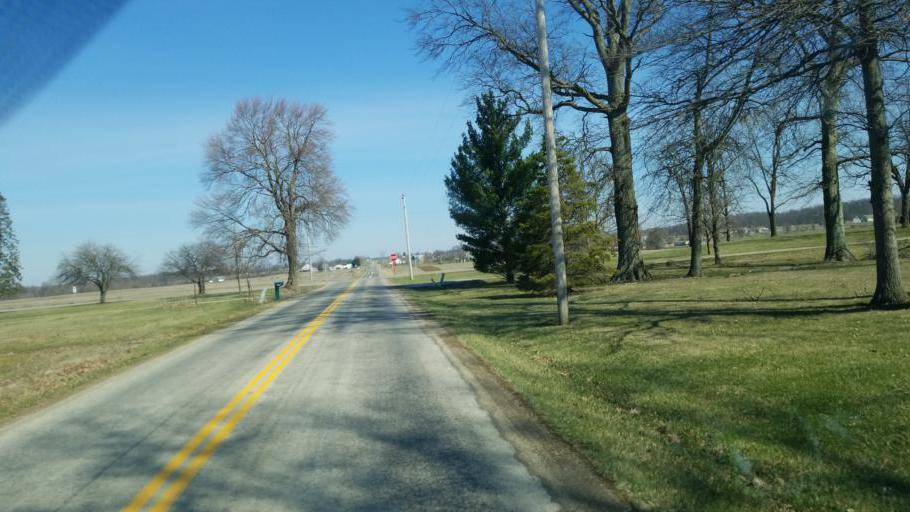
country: US
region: Ohio
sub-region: Ashland County
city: Ashland
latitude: 40.9223
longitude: -82.2432
